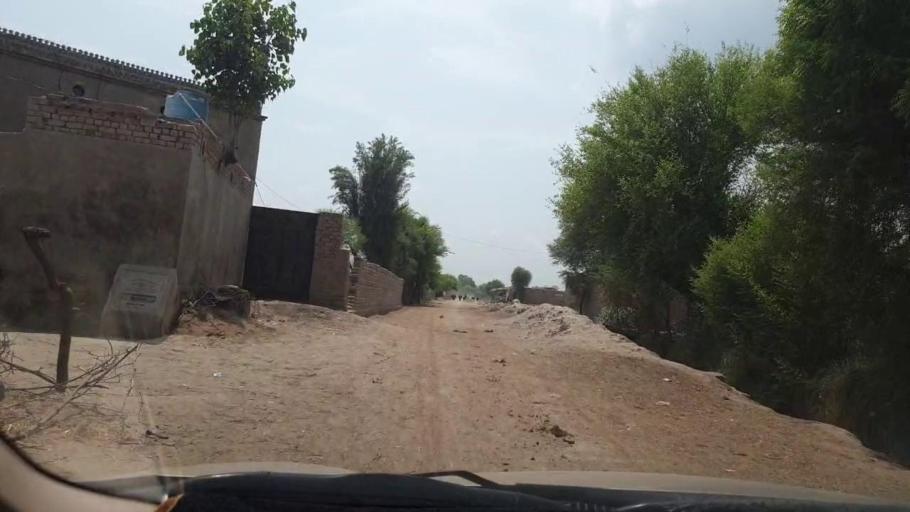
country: PK
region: Sindh
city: Larkana
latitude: 27.6072
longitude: 68.1280
